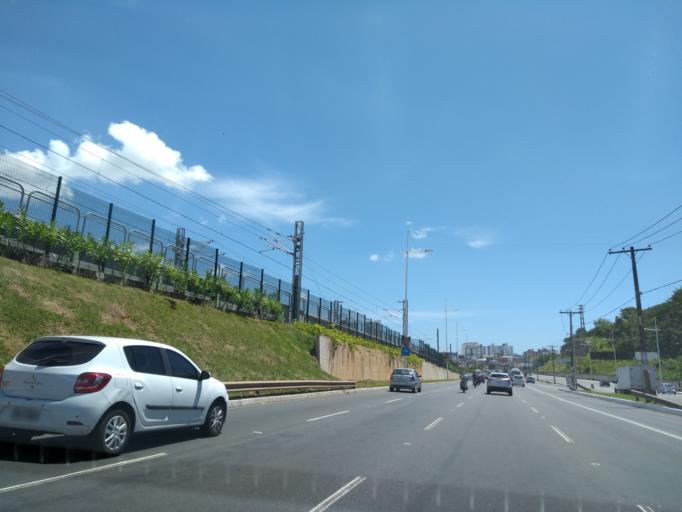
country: BR
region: Bahia
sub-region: Salvador
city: Salvador
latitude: -12.9725
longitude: -38.4470
